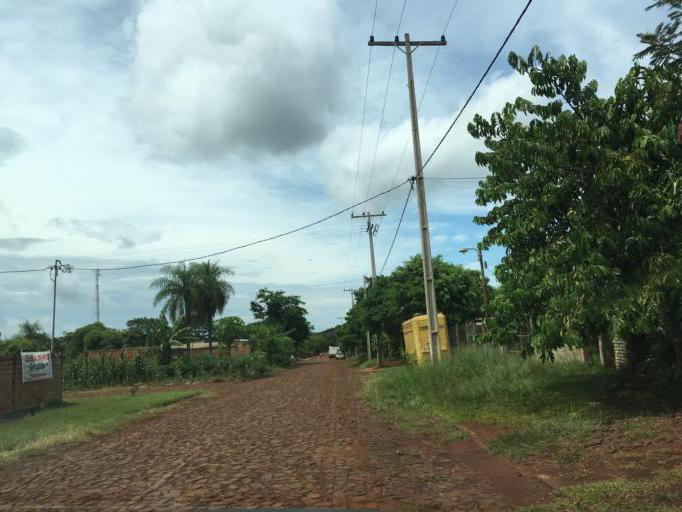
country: PY
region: Alto Parana
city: Ciudad del Este
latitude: -25.4252
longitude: -54.6396
